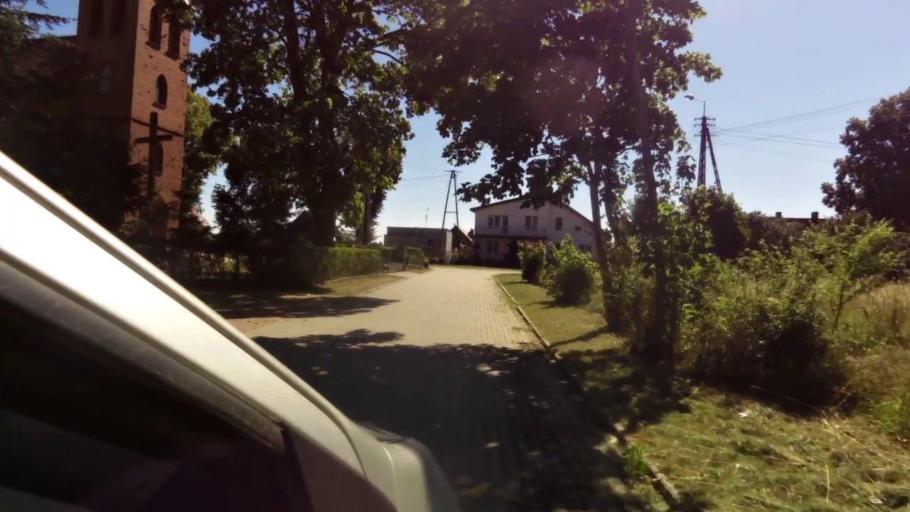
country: PL
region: West Pomeranian Voivodeship
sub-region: Powiat szczecinecki
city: Bialy Bor
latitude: 53.8144
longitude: 16.8477
